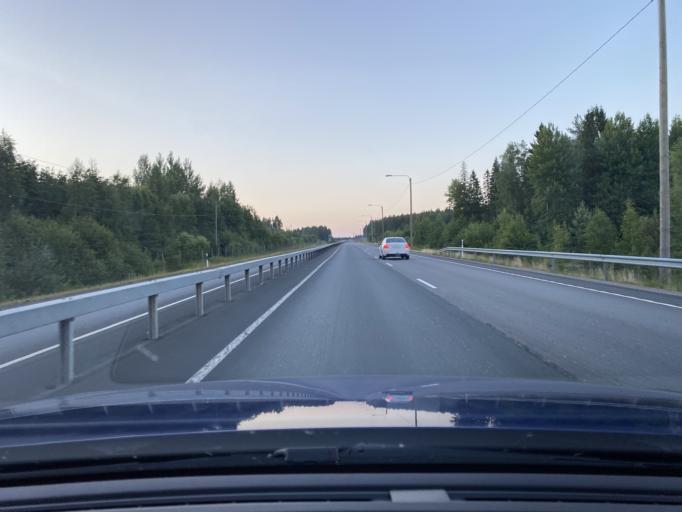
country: FI
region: Pirkanmaa
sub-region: Luoteis-Pirkanmaa
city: Parkano
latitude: 61.8838
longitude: 22.9731
